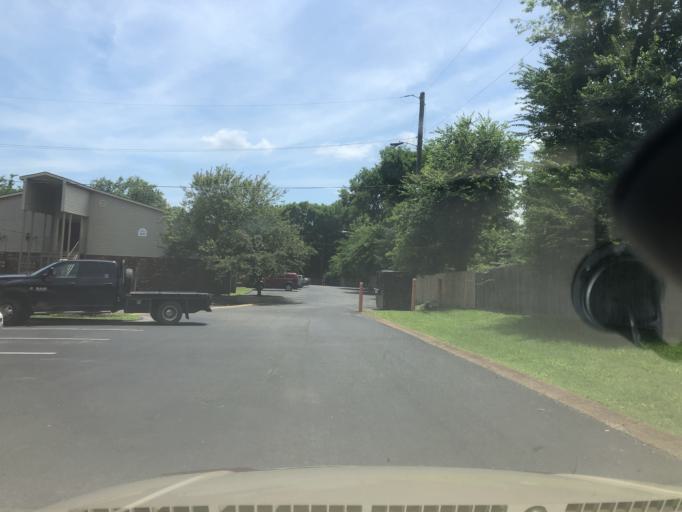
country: US
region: Tennessee
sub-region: Davidson County
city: Goodlettsville
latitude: 36.2584
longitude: -86.7063
